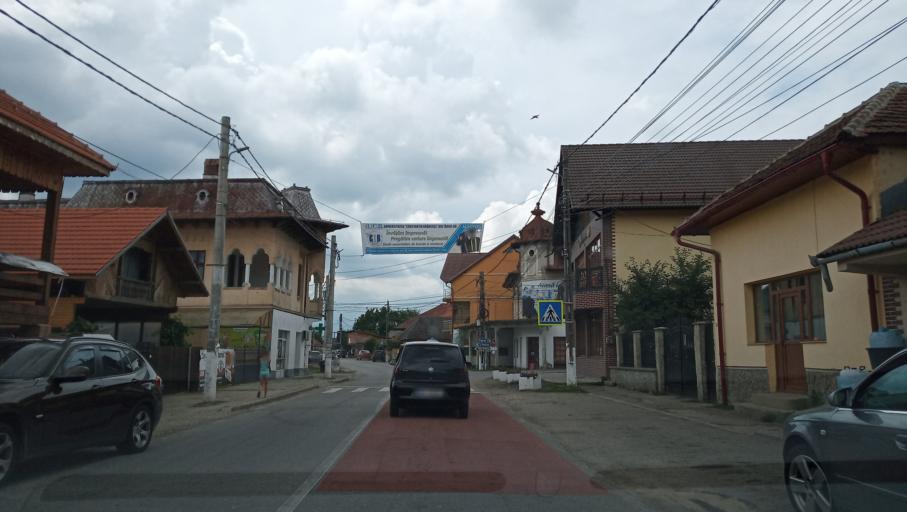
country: RO
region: Gorj
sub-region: Comuna Pestisani
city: Pestisani
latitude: 45.0784
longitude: 23.0462
